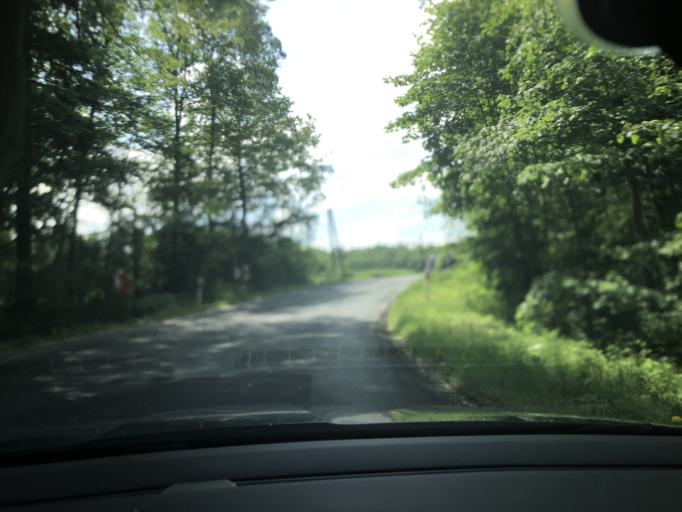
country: PL
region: Lower Silesian Voivodeship
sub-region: Powiat zlotoryjski
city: Swierzawa
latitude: 50.9823
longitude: 15.8824
